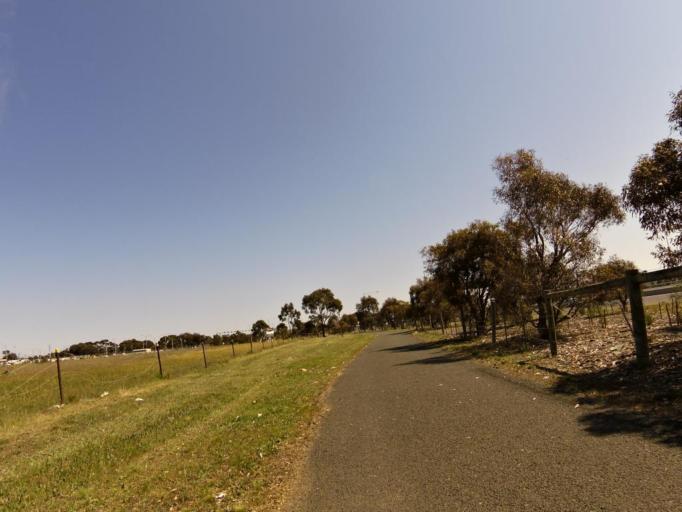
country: AU
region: Victoria
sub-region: Brimbank
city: Cairnlea
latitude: -37.7676
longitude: 144.8018
